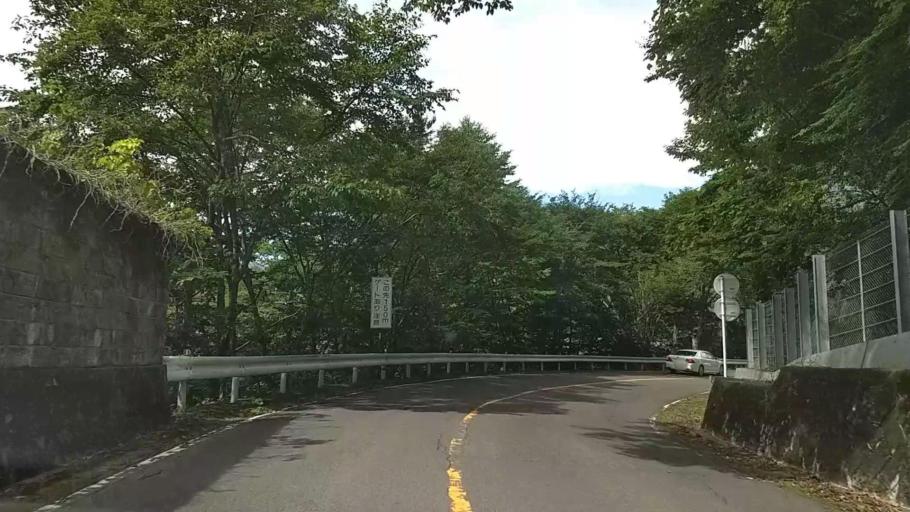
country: JP
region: Tochigi
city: Nikko
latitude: 36.7277
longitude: 139.4855
